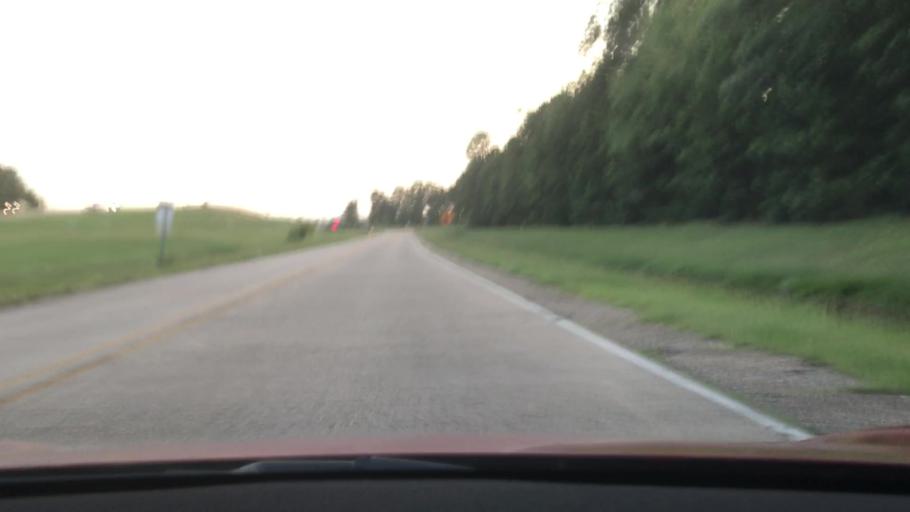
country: US
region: Louisiana
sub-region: Bossier Parish
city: Bossier City
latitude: 32.4032
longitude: -93.7334
